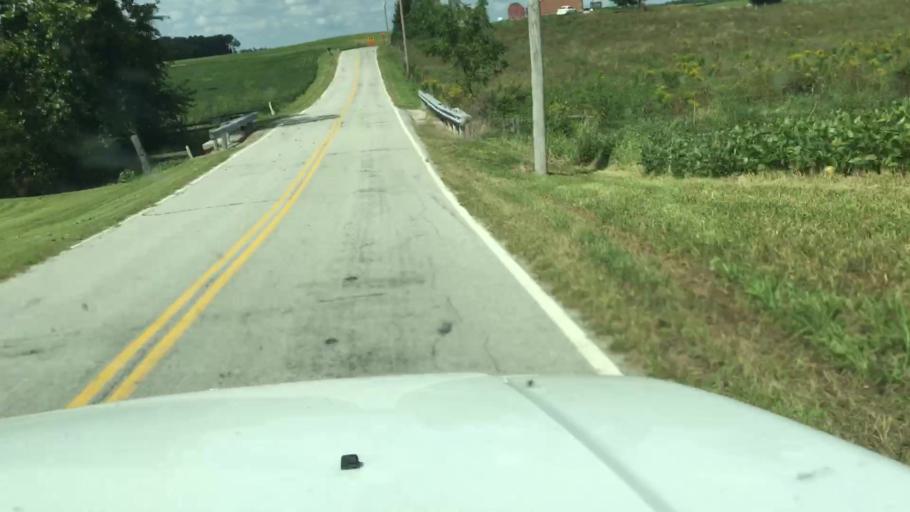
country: US
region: Ohio
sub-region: Madison County
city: Choctaw Lake
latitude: 39.9472
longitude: -83.5695
